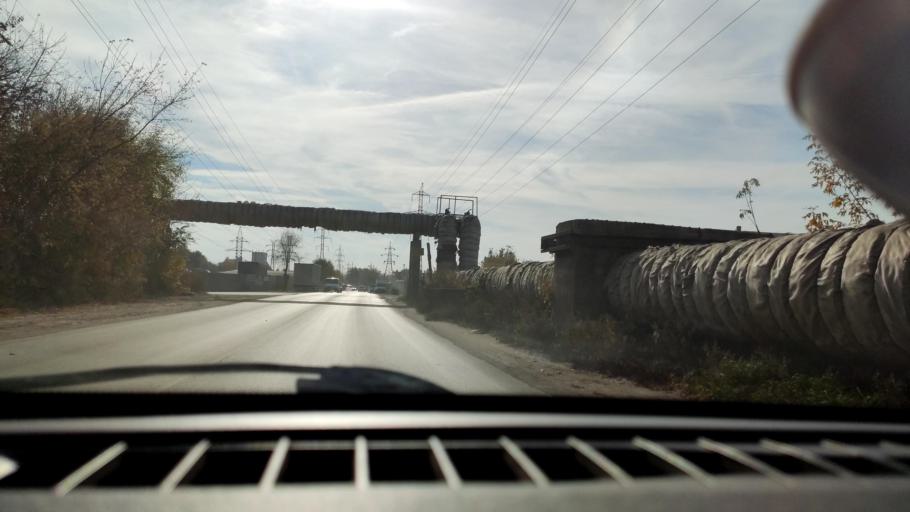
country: RU
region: Samara
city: Petra-Dubrava
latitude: 53.2557
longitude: 50.2959
